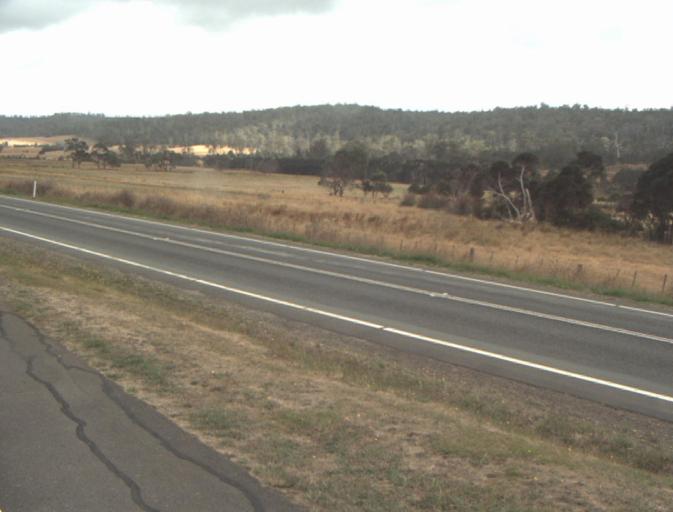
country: AU
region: Tasmania
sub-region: Launceston
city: Mayfield
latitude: -41.3252
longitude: 147.0643
